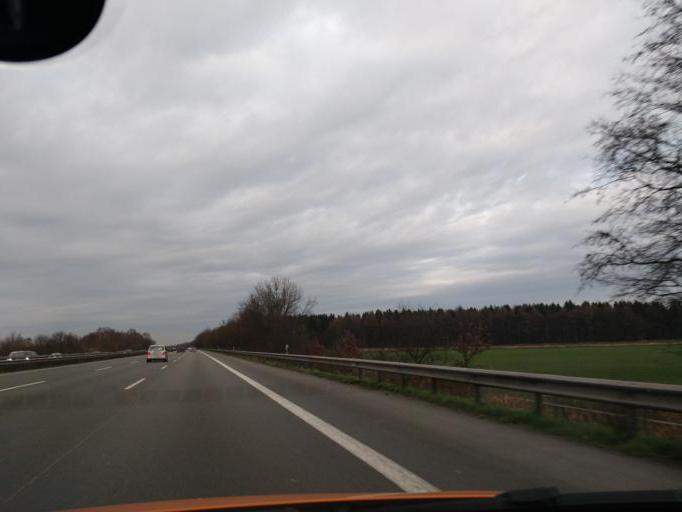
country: DE
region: Lower Saxony
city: Essel
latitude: 52.7221
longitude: 9.6805
